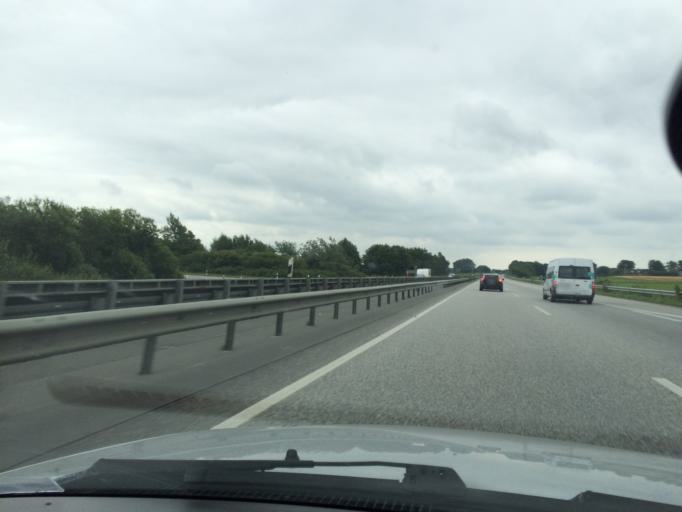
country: DE
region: Schleswig-Holstein
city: Jarplund-Weding
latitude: 54.7335
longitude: 9.3894
